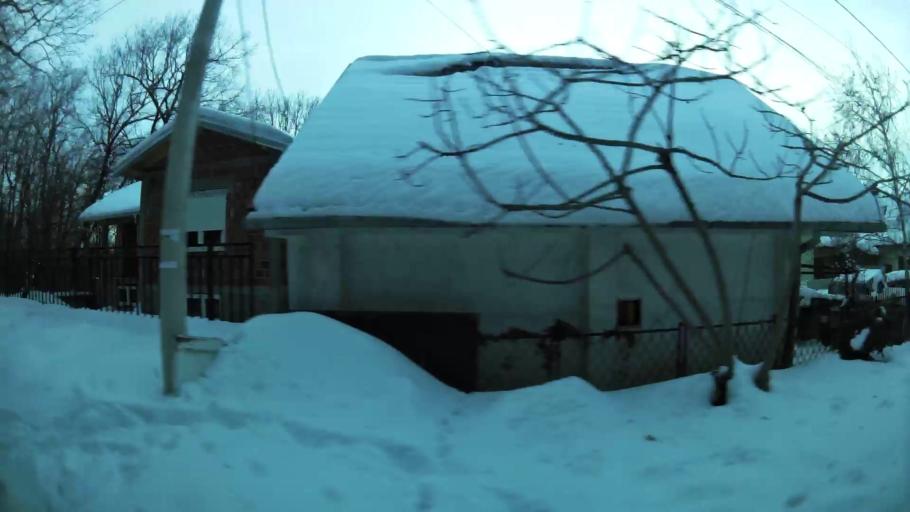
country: RS
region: Central Serbia
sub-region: Belgrade
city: Palilula
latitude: 44.8020
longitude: 20.5052
